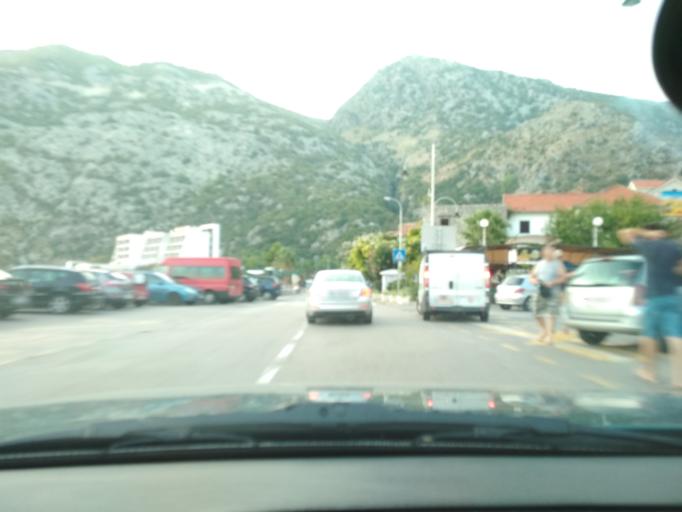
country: ME
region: Kotor
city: Risan
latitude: 42.5147
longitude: 18.6940
